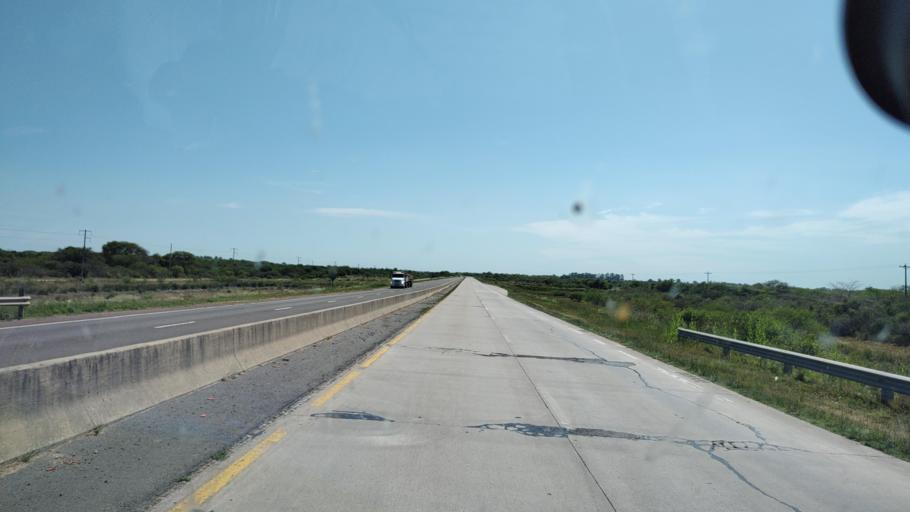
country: AR
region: Entre Rios
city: Gualeguaychu
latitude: -32.9686
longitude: -58.5888
